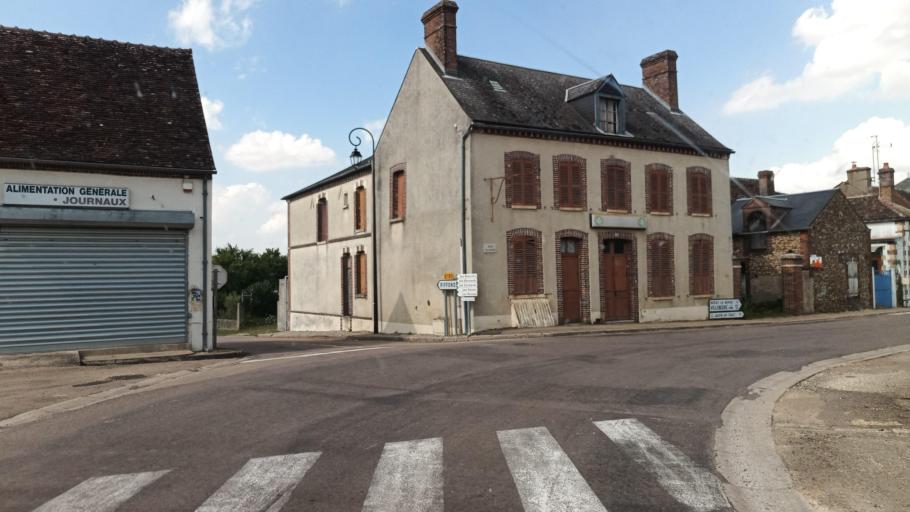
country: FR
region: Bourgogne
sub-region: Departement de l'Yonne
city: Egriselles-le-Bocage
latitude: 48.0233
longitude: 3.1757
